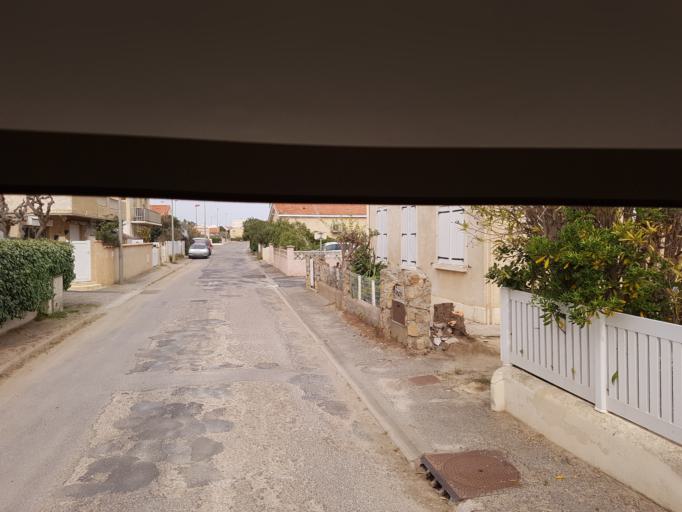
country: FR
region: Languedoc-Roussillon
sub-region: Departement de l'Aude
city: Fleury
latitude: 43.1675
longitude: 3.1770
